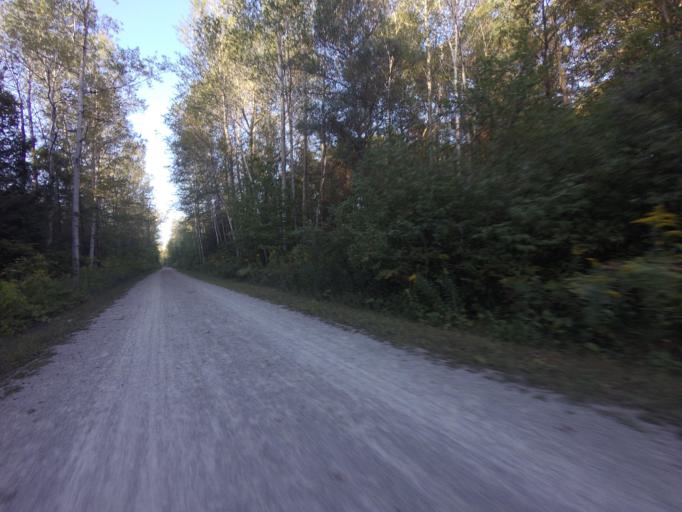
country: CA
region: Ontario
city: Brampton
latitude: 43.8485
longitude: -79.8806
